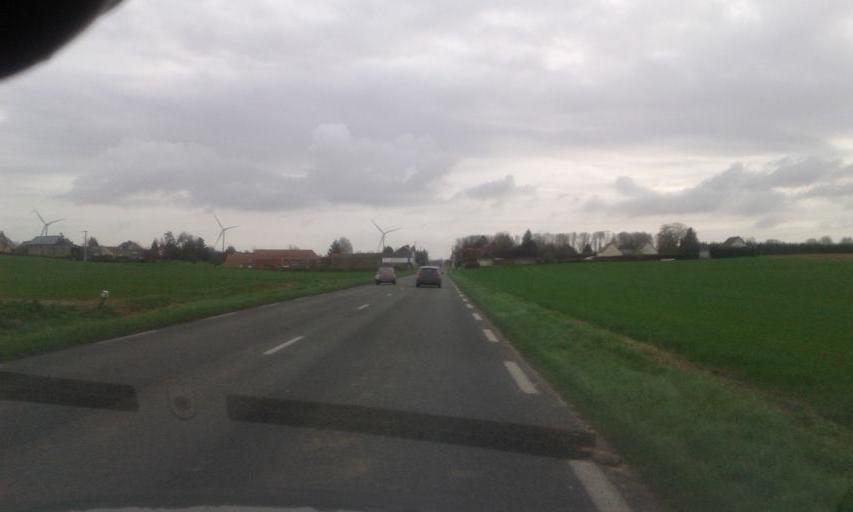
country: FR
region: Haute-Normandie
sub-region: Departement de la Seine-Maritime
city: Montmain
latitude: 49.3860
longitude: 1.2666
